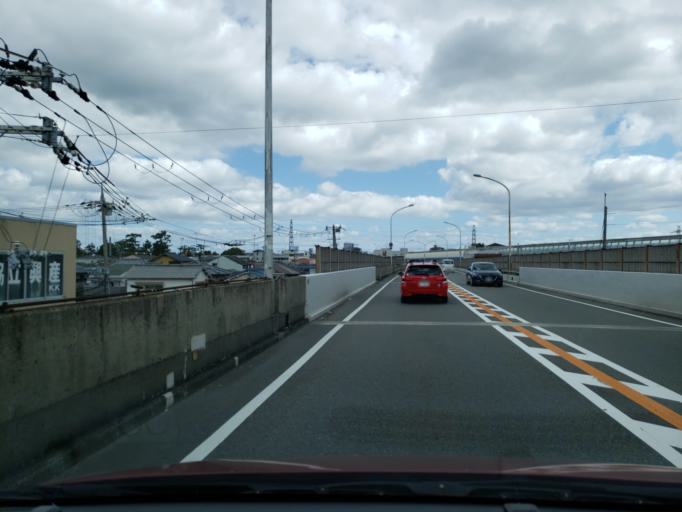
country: JP
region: Osaka
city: Toyonaka
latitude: 34.7578
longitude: 135.4763
